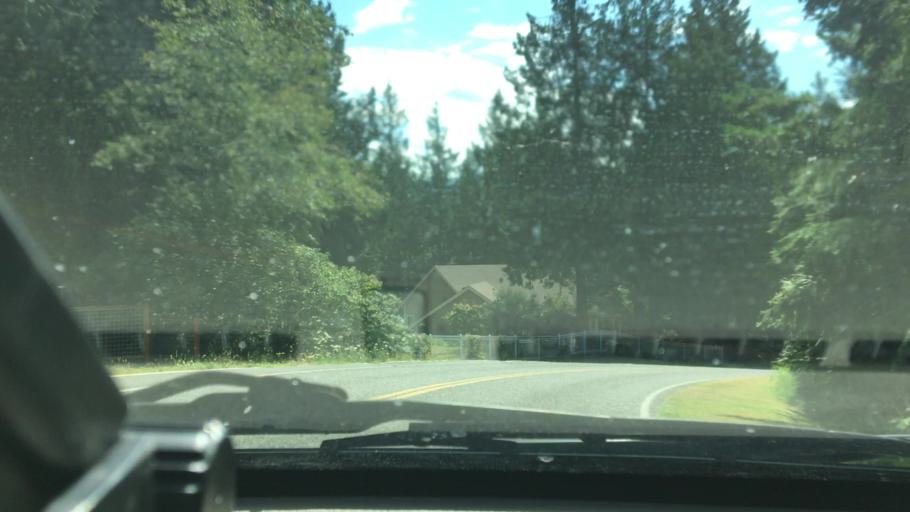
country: US
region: Washington
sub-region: Whatcom County
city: Geneva
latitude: 48.7626
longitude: -122.3653
